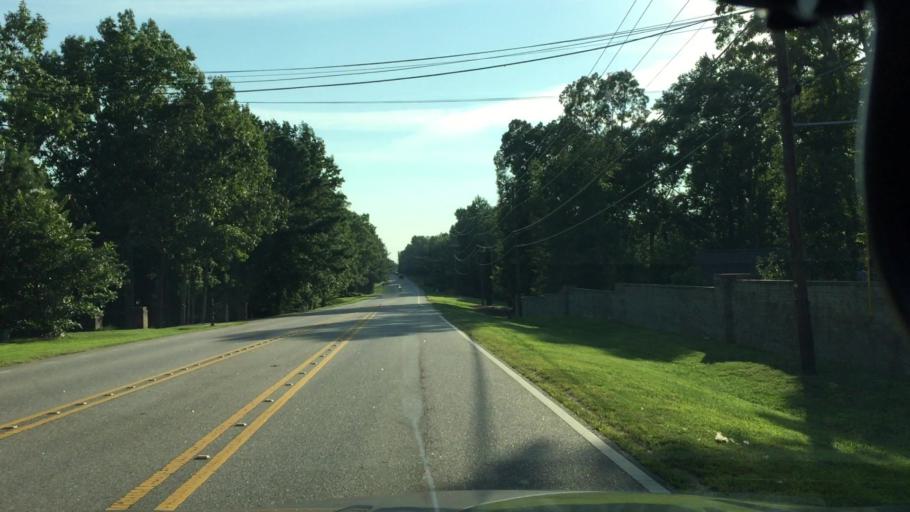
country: US
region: Alabama
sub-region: Lee County
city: Auburn
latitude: 32.5965
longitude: -85.4197
